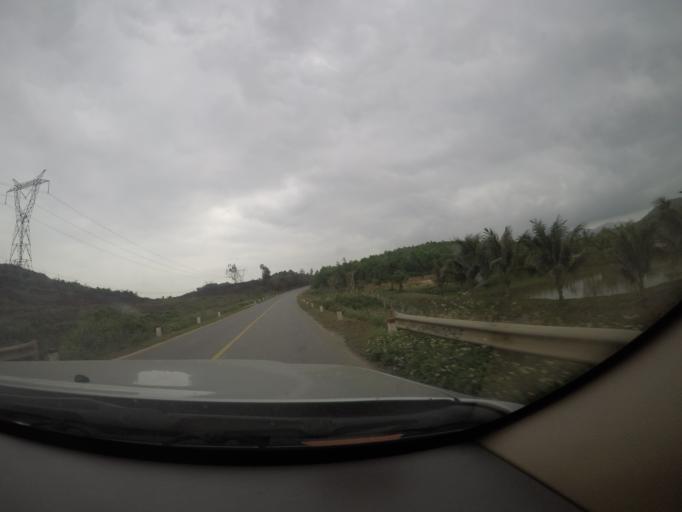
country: VN
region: Quang Binh
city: Hoan Lao
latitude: 17.6113
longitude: 106.4052
